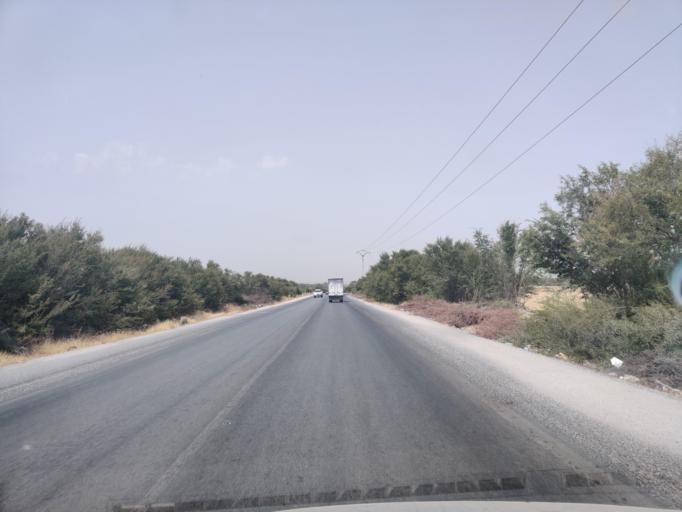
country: TN
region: Tunis
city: La Sebala du Mornag
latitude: 36.6497
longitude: 10.3419
